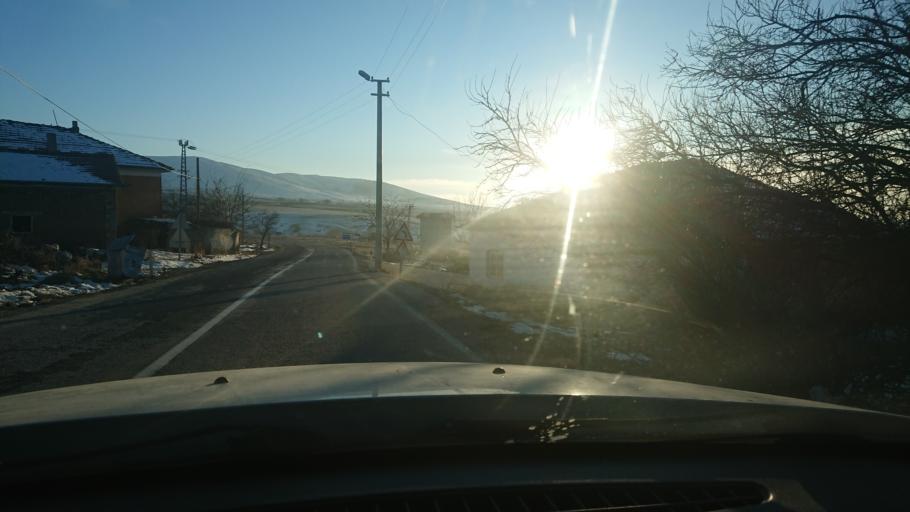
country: TR
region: Aksaray
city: Ortakoy
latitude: 38.7559
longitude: 33.9338
